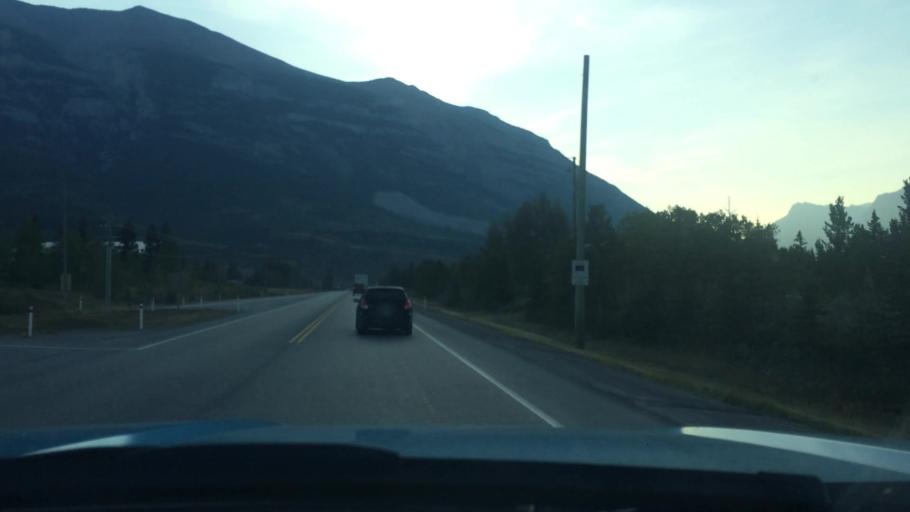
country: CA
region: Alberta
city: Canmore
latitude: 51.0750
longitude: -115.3280
